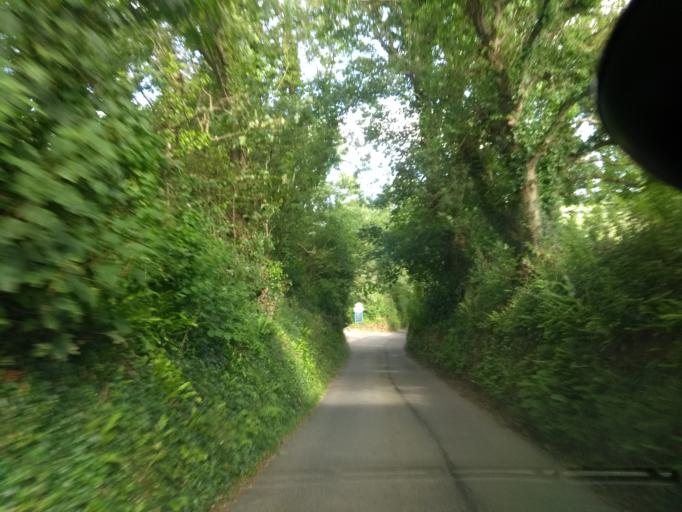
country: GB
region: England
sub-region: Devon
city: Modbury
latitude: 50.3066
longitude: -3.8554
